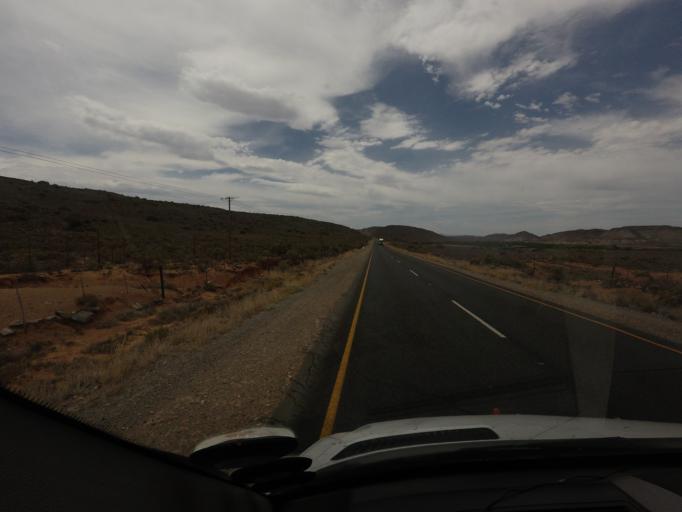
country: ZA
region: Western Cape
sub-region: Eden District Municipality
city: Riversdale
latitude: -33.7989
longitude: 20.9160
